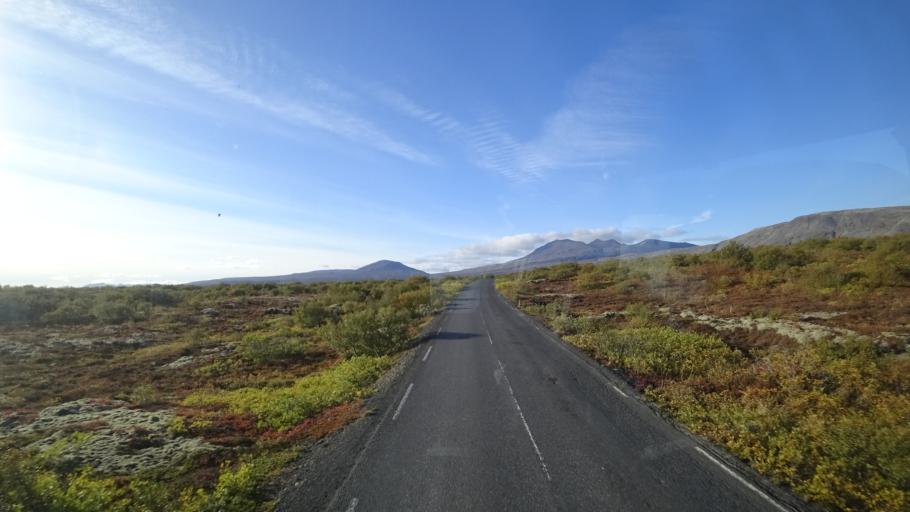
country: IS
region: South
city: Hveragerdi
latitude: 64.2662
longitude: -21.0599
